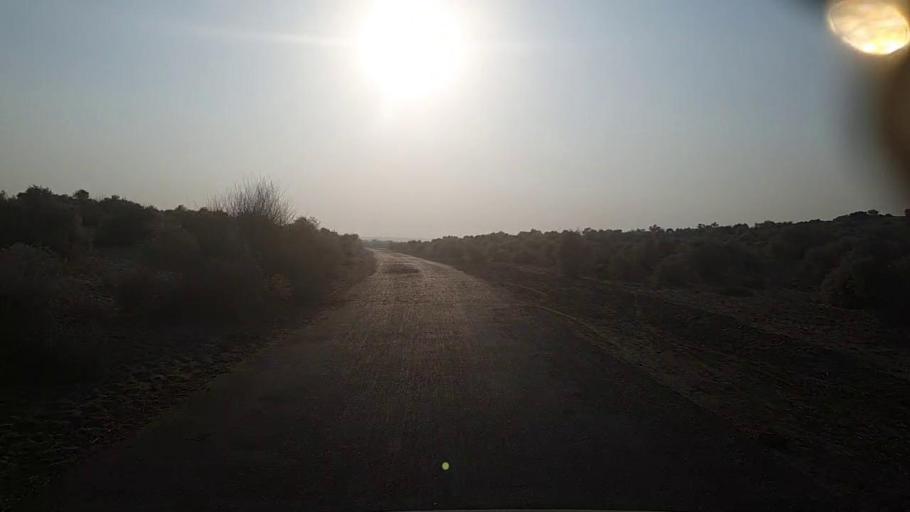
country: PK
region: Sindh
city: Pad Idan
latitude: 26.7223
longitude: 68.4395
